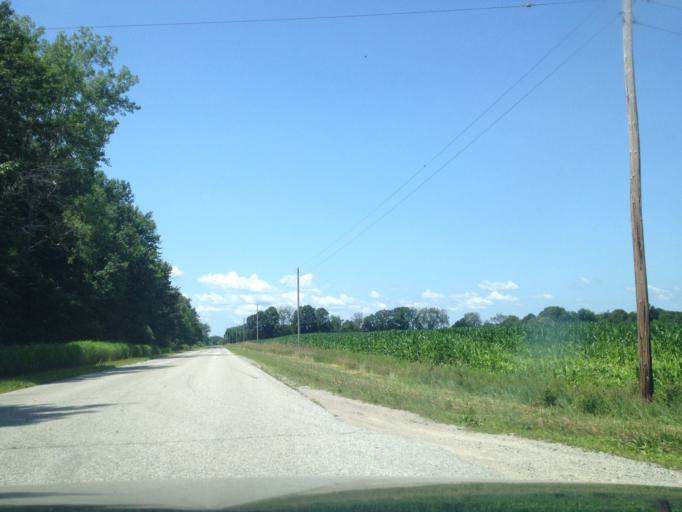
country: CA
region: Ontario
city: Aylmer
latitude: 42.6426
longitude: -80.7804
